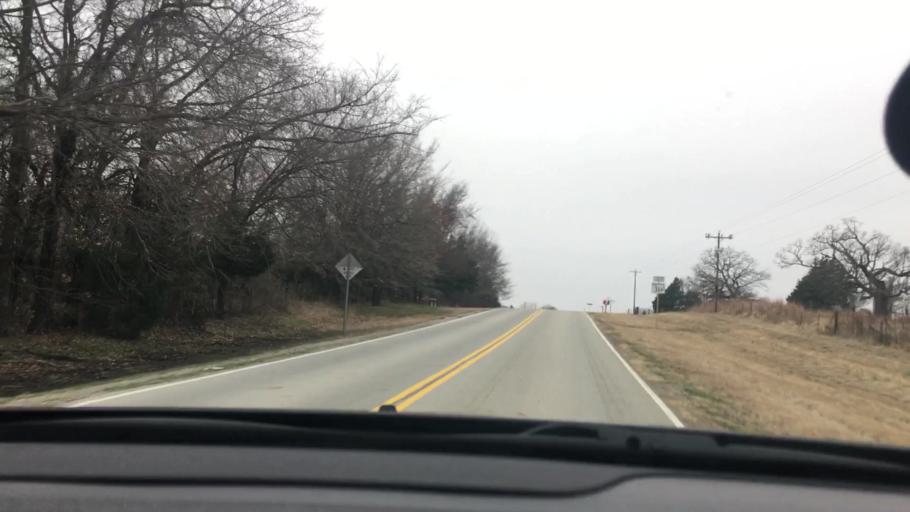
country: US
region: Oklahoma
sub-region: Coal County
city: Coalgate
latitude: 34.5055
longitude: -96.3685
